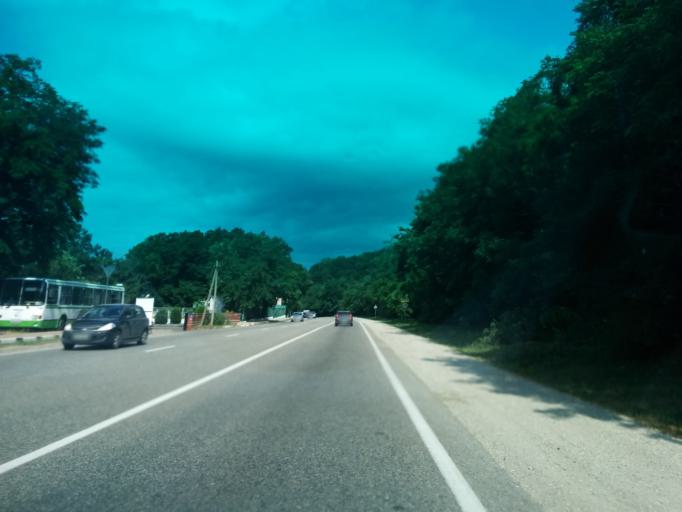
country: RU
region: Krasnodarskiy
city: Nebug
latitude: 44.1689
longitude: 38.9860
